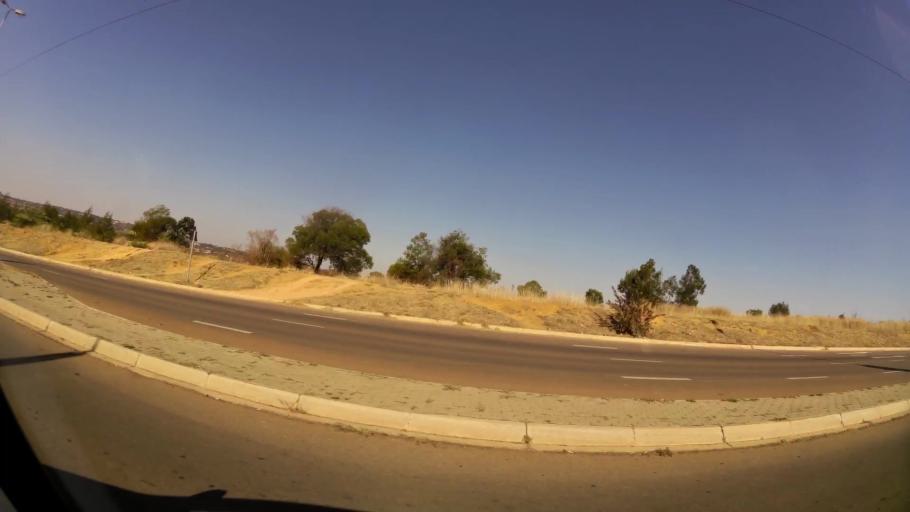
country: ZA
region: Gauteng
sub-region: City of Tshwane Metropolitan Municipality
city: Centurion
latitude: -25.8251
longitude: 28.3075
